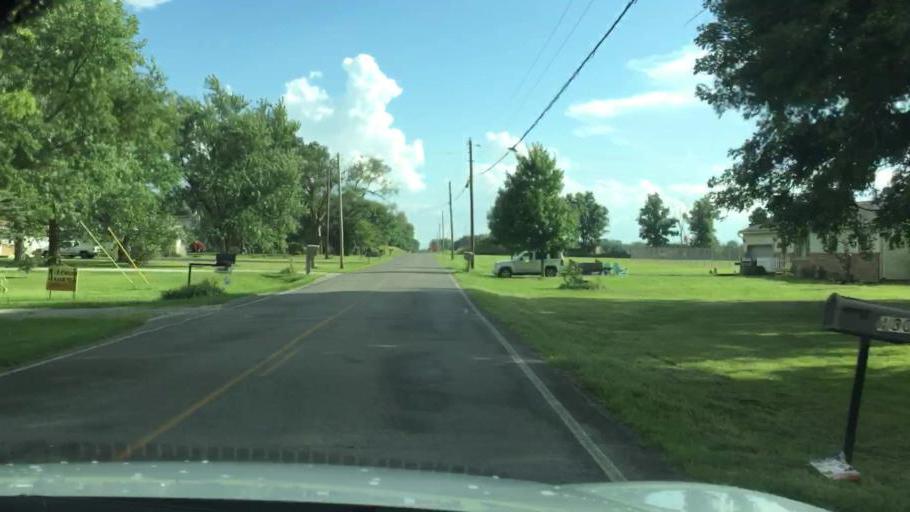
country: US
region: Ohio
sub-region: Champaign County
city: Urbana
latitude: 40.1045
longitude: -83.7126
